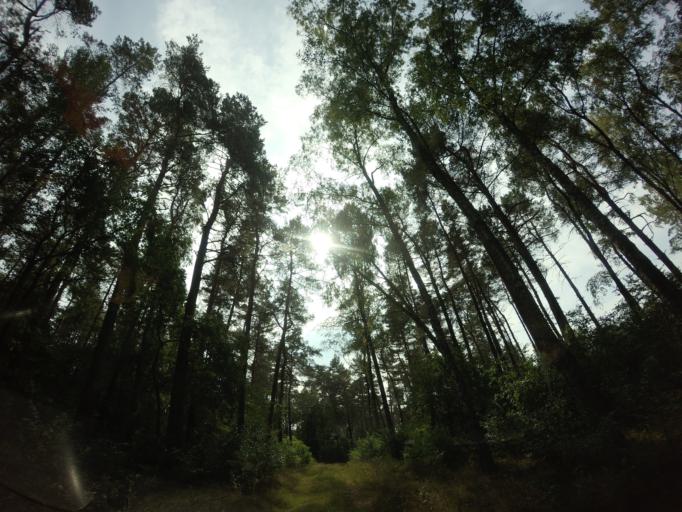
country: PL
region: West Pomeranian Voivodeship
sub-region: Powiat drawski
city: Drawsko Pomorskie
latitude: 53.4610
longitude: 15.7145
